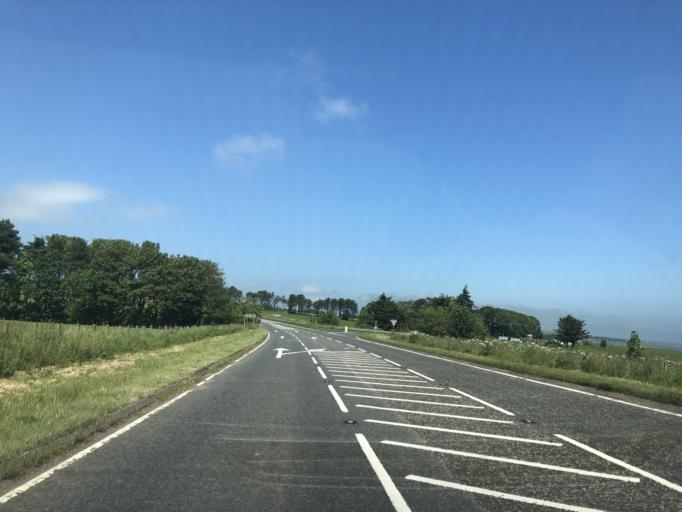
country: GB
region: Scotland
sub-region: Aberdeenshire
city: Stonehaven
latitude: 56.9411
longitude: -2.2074
